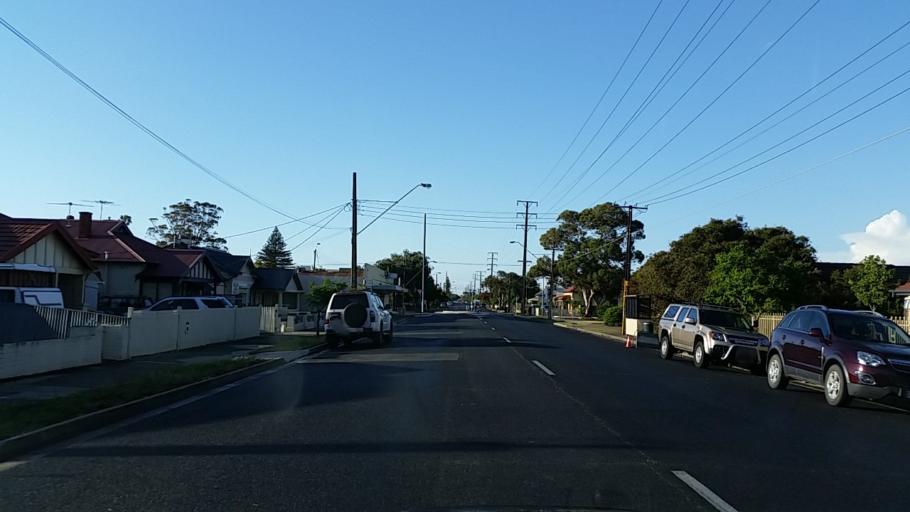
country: AU
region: South Australia
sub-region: Port Adelaide Enfield
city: Birkenhead
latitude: -34.8306
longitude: 138.4963
